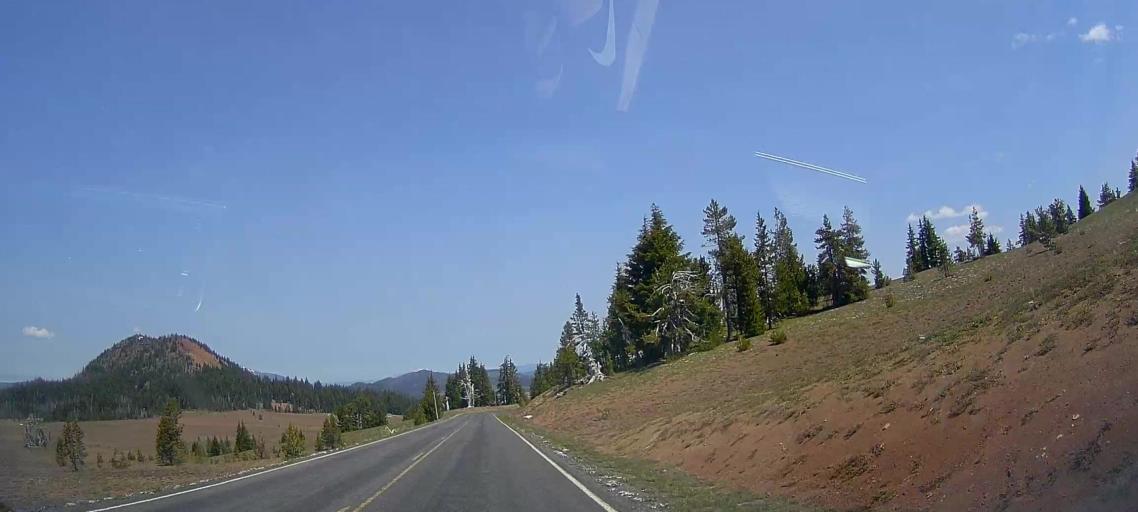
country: US
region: Oregon
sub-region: Jackson County
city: Shady Cove
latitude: 42.9805
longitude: -122.1527
